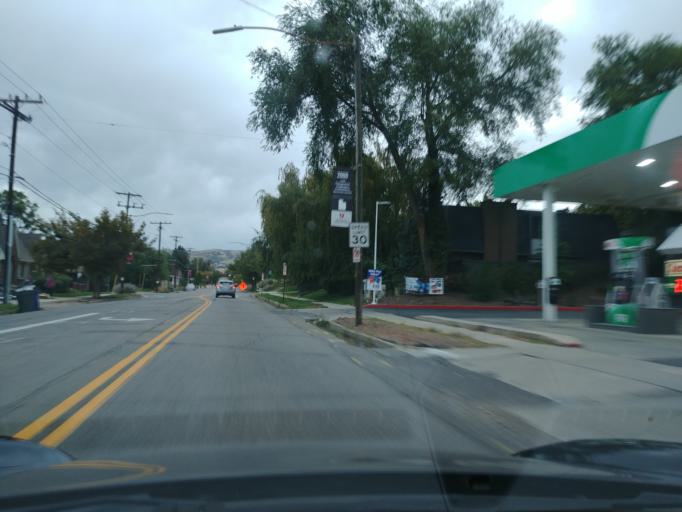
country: US
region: Utah
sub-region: Salt Lake County
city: Willard
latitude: 40.7336
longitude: -111.8538
